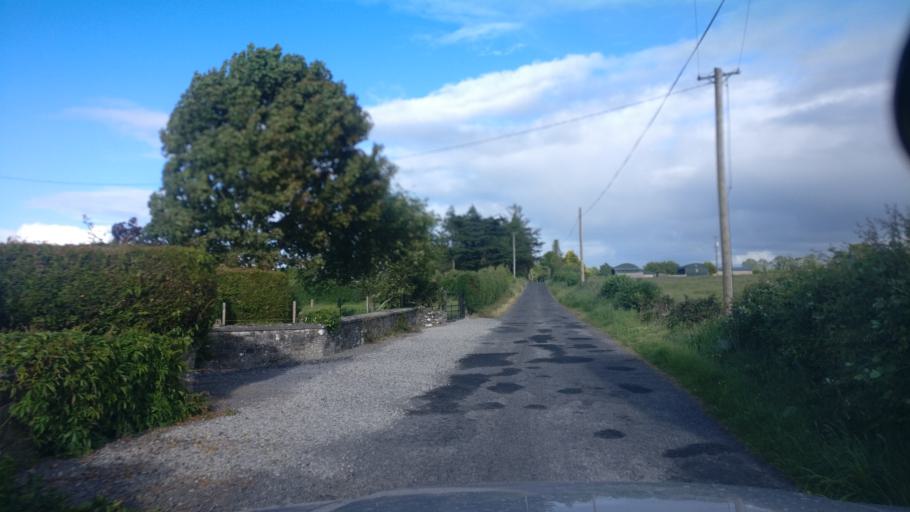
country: IE
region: Connaught
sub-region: County Galway
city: Ballinasloe
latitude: 53.2456
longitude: -8.2105
